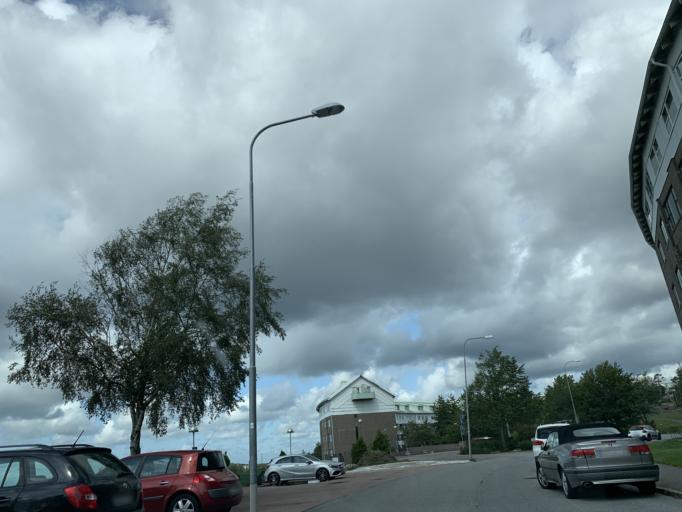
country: SE
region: Vaestra Goetaland
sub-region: Goteborg
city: Eriksbo
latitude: 57.7619
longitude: 12.0580
